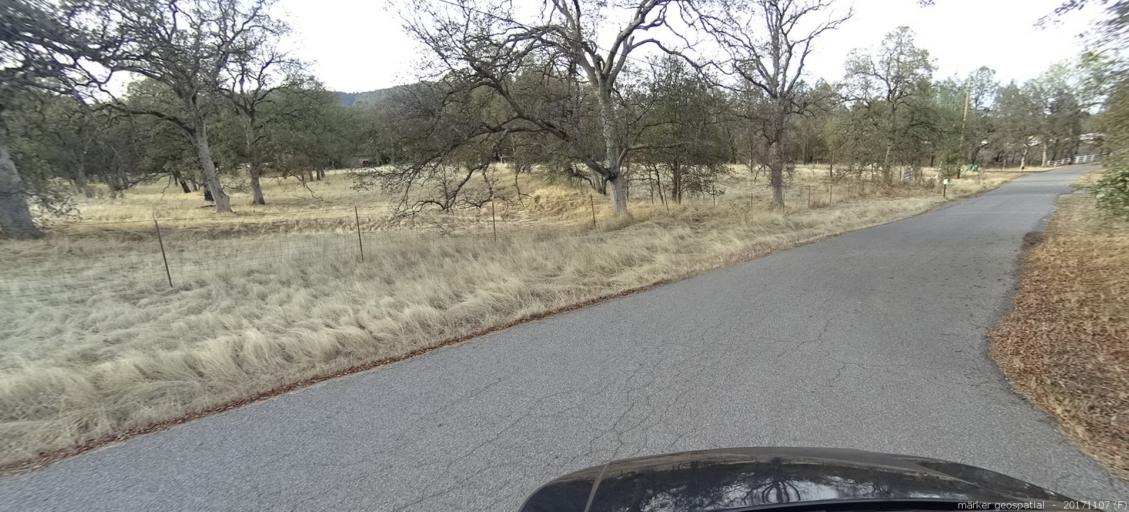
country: US
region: California
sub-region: Shasta County
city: Shasta
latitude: 40.5224
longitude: -122.4783
